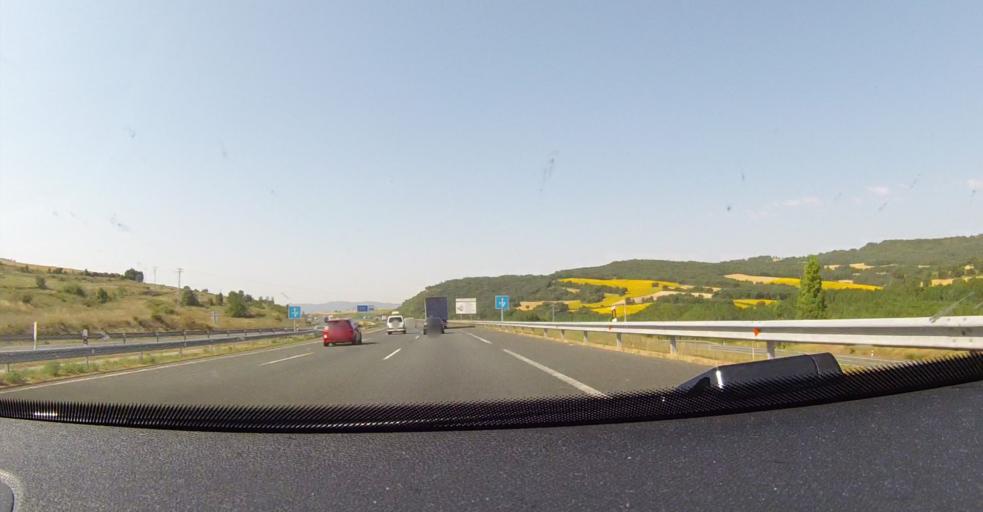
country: ES
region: Basque Country
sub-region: Provincia de Alava
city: Arminon
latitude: 42.7390
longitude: -2.8688
